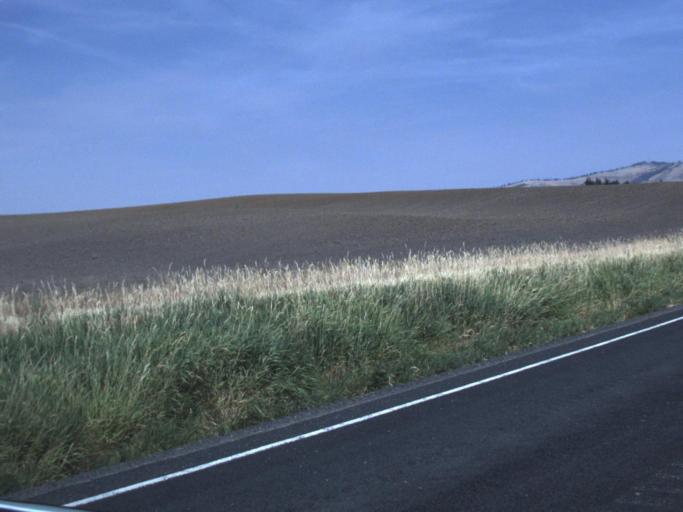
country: US
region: Idaho
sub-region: Benewah County
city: Plummer
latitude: 47.1934
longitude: -117.1458
